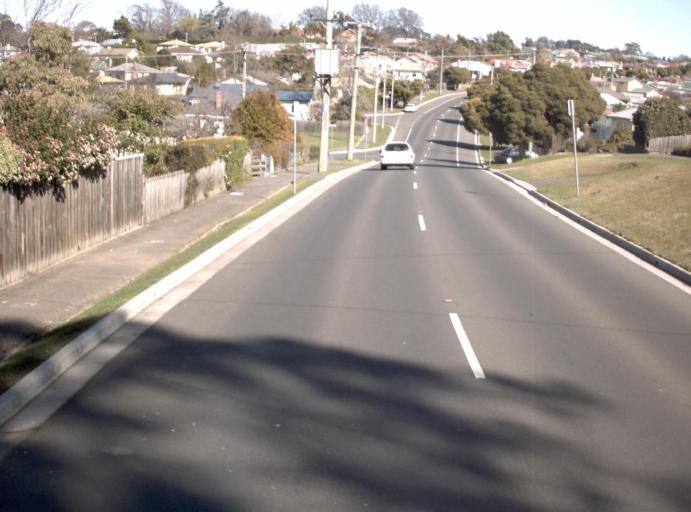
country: AU
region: Tasmania
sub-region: Launceston
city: East Launceston
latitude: -41.4575
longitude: 147.1648
